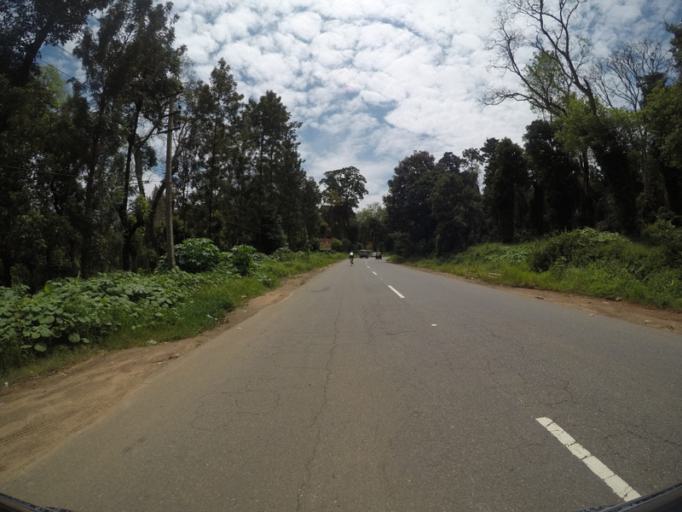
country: IN
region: Karnataka
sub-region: Kodagu
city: Suntikoppa
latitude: 12.4528
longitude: 75.8342
